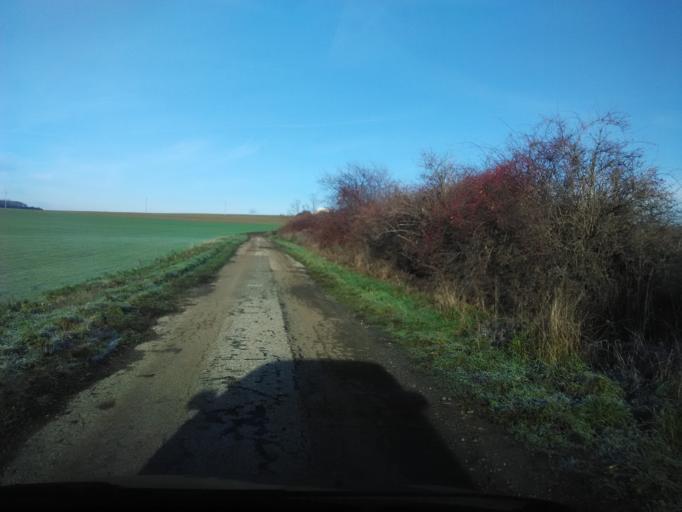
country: SK
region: Nitriansky
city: Tlmace
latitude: 48.3350
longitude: 18.5323
